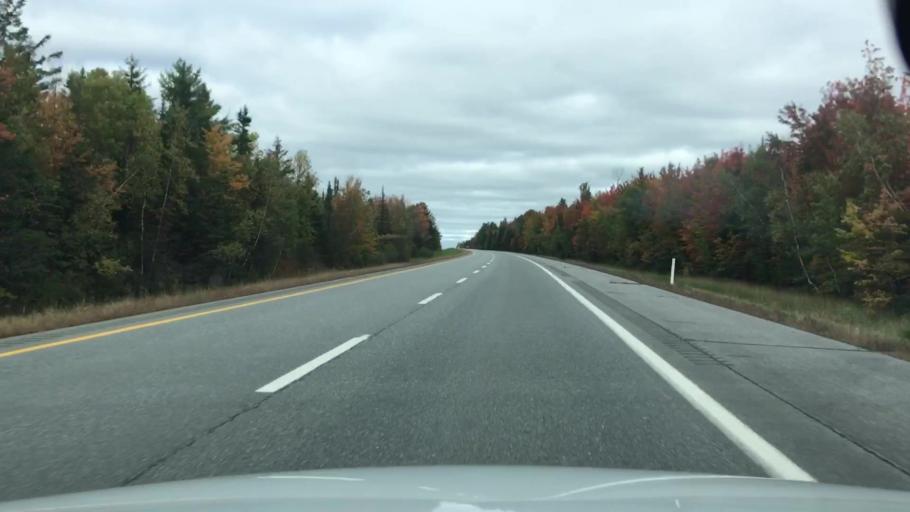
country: US
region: Maine
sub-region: Kennebec County
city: Clinton
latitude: 44.6679
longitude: -69.4892
